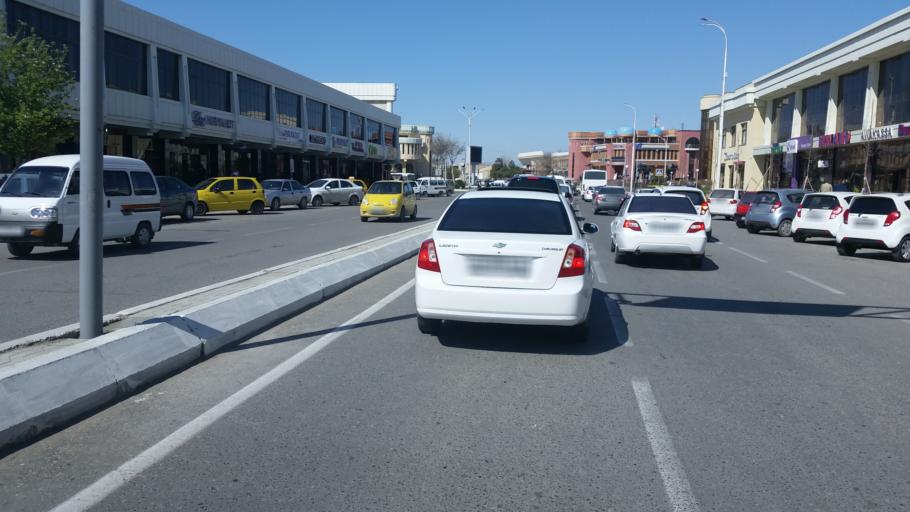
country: UZ
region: Bukhara
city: Bukhara
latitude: 39.7733
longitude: 64.4335
